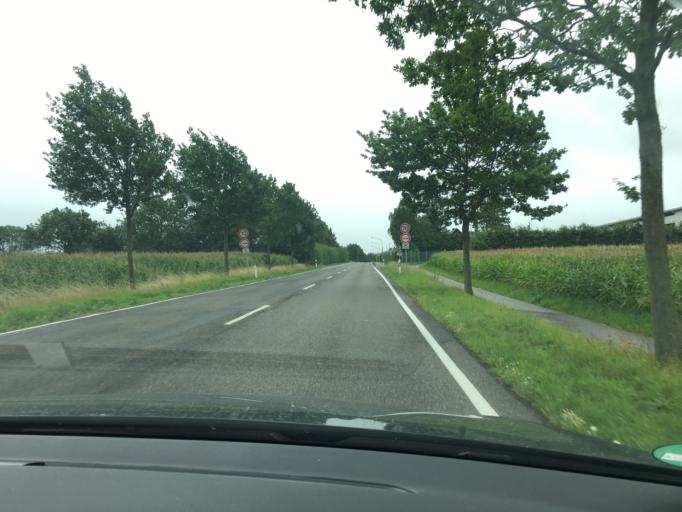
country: DE
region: North Rhine-Westphalia
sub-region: Regierungsbezirk Koln
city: Hurtgenwald
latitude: 50.6984
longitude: 6.3588
